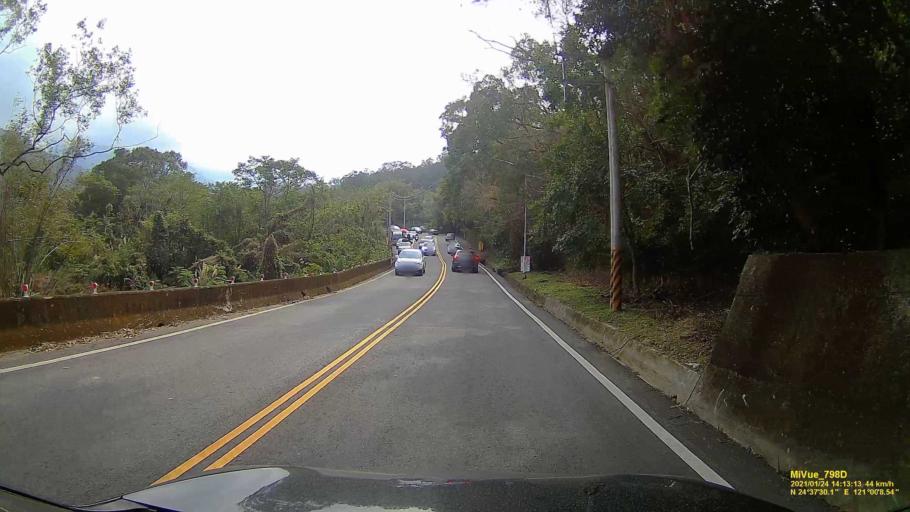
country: TW
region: Taiwan
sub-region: Hsinchu
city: Hsinchu
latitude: 24.6248
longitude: 121.0023
